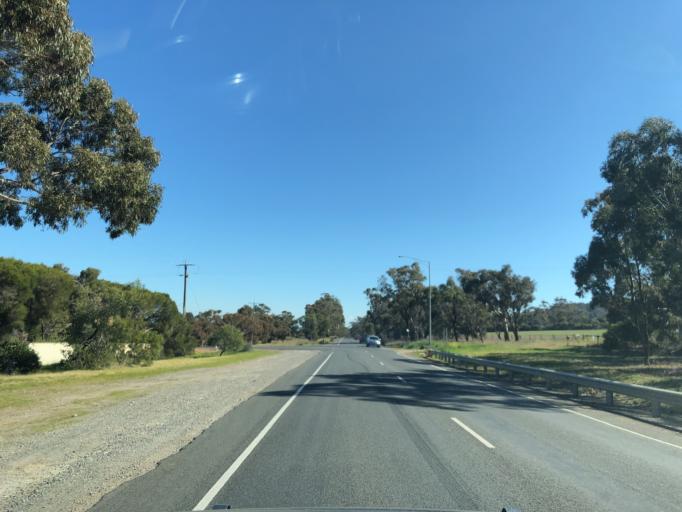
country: AU
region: Victoria
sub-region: Melton
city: Melton West
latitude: -37.6118
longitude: 144.5694
